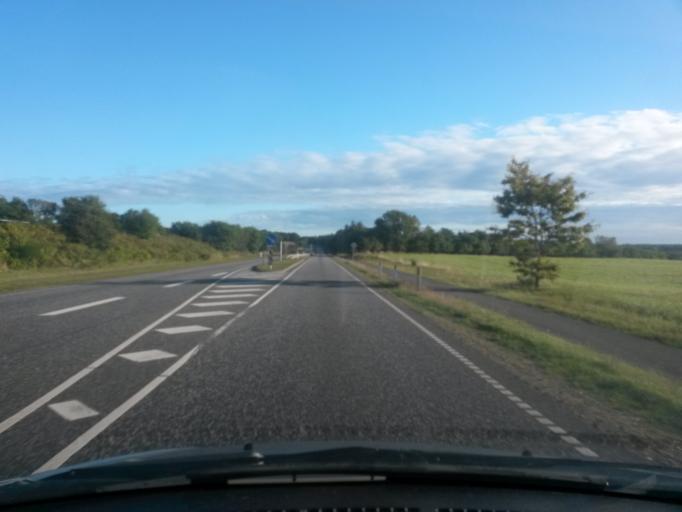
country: DK
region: Central Jutland
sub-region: Viborg Kommune
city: Viborg
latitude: 56.4191
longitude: 9.3832
